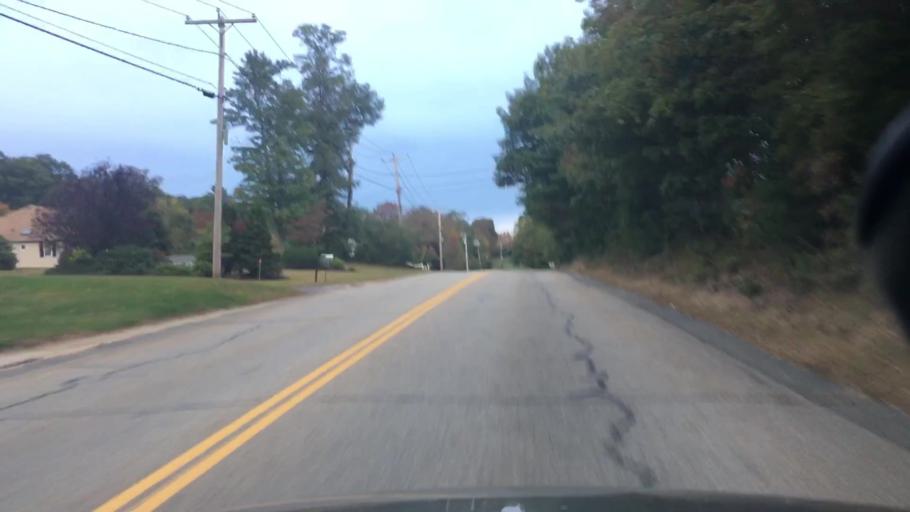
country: US
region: Massachusetts
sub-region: Worcester County
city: Charlton
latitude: 42.1313
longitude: -71.9645
